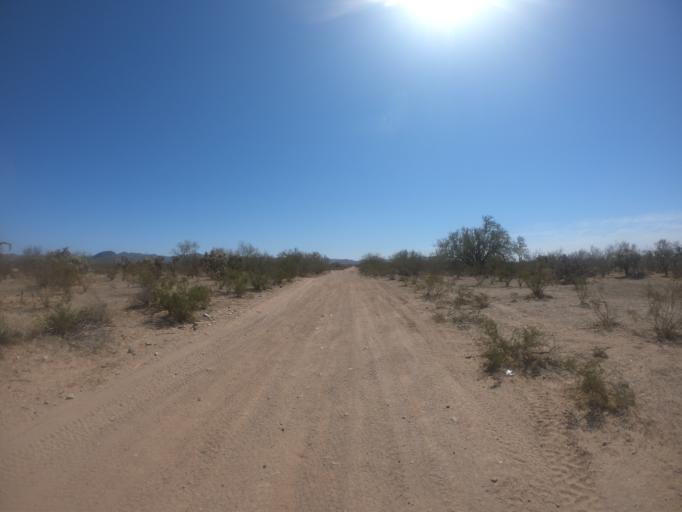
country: US
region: Arizona
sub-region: Pinal County
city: Gold Camp
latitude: 33.2395
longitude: -111.3129
